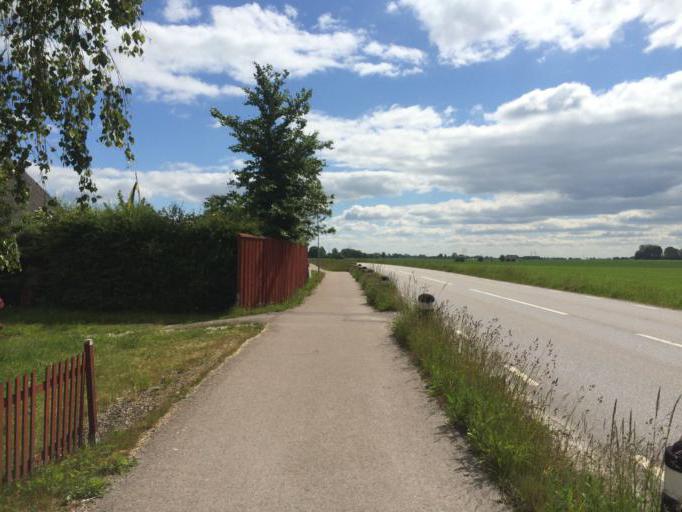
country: SE
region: Skane
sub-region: Lomma Kommun
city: Lomma
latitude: 55.6736
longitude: 13.1036
